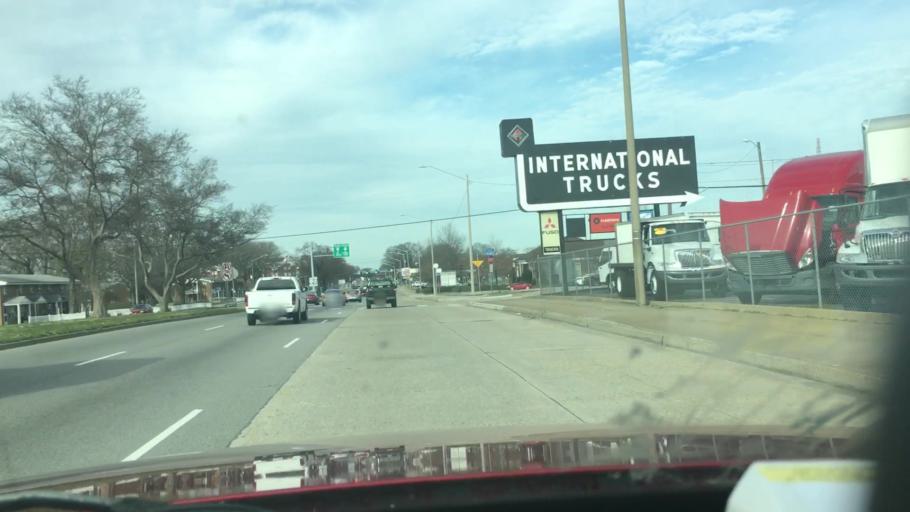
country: US
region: Virginia
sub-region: City of Norfolk
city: Norfolk
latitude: 36.8517
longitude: -76.2756
